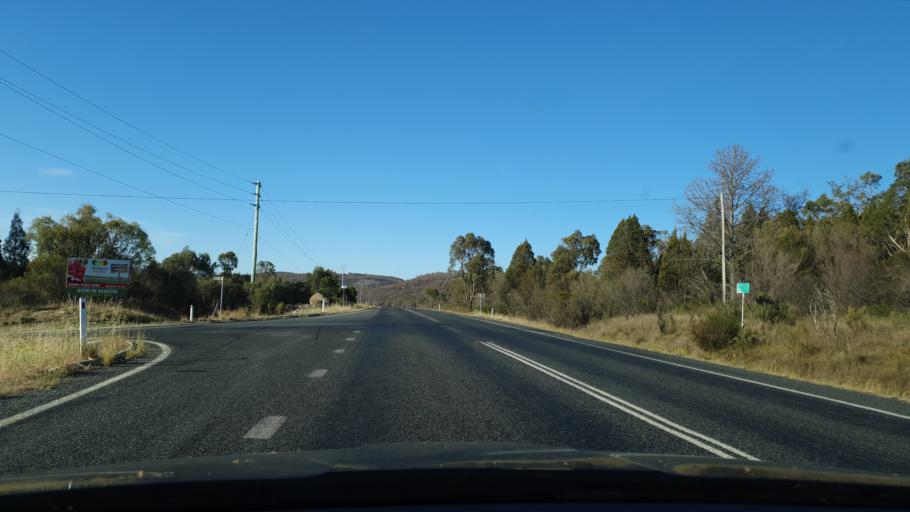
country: AU
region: Queensland
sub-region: Southern Downs
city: Stanthorpe
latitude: -28.6621
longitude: 151.9161
